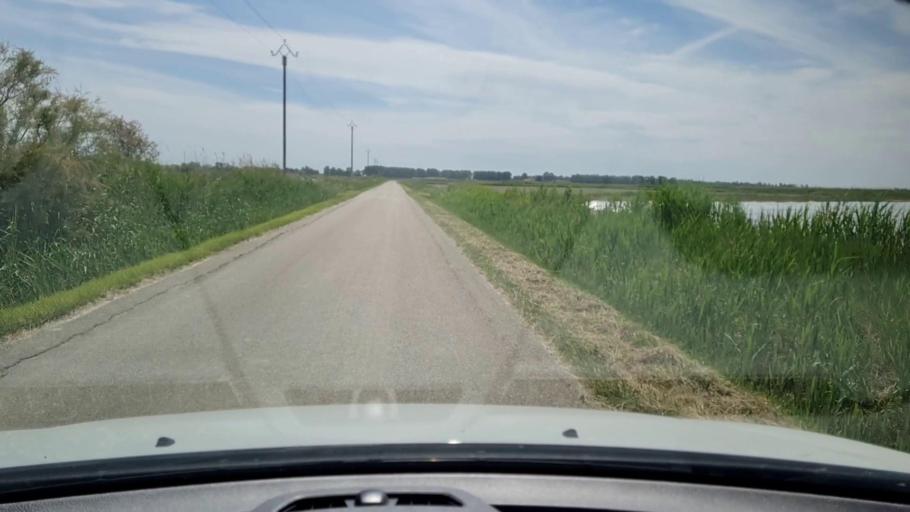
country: FR
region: Languedoc-Roussillon
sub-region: Departement du Gard
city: Saint-Gilles
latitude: 43.5949
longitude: 4.4581
